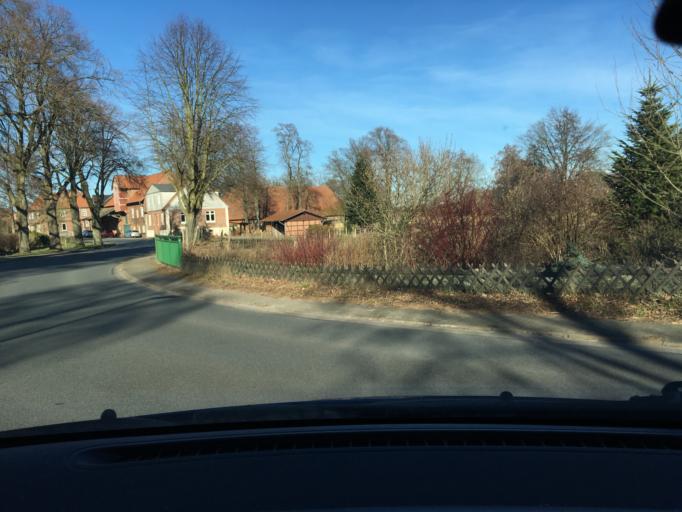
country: DE
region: Lower Saxony
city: Hanstedt Eins
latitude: 53.0435
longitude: 10.3762
